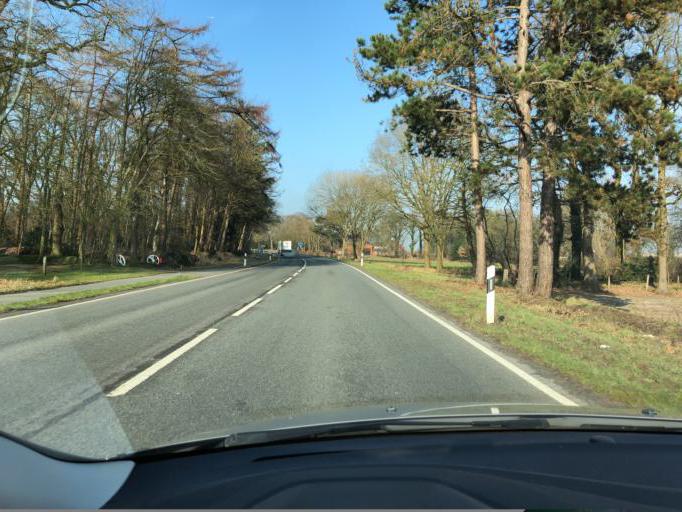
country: DE
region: Lower Saxony
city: Westerstede
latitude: 53.2894
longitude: 7.8893
